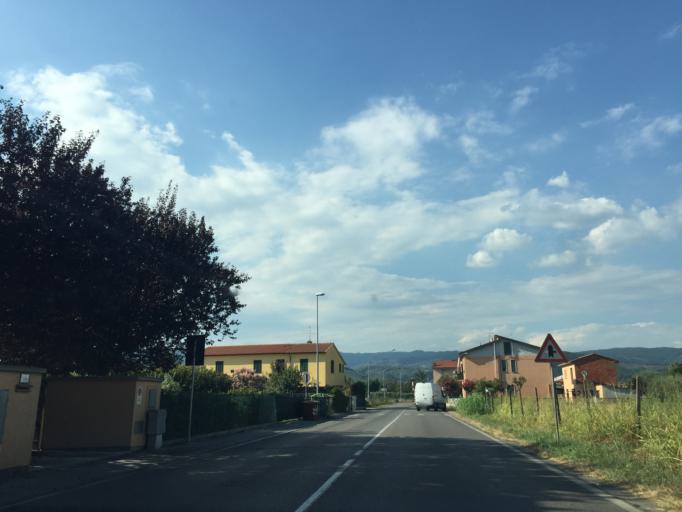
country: IT
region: Tuscany
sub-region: Provincia di Pistoia
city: Pieve a Nievole
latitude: 43.8668
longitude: 10.7981
